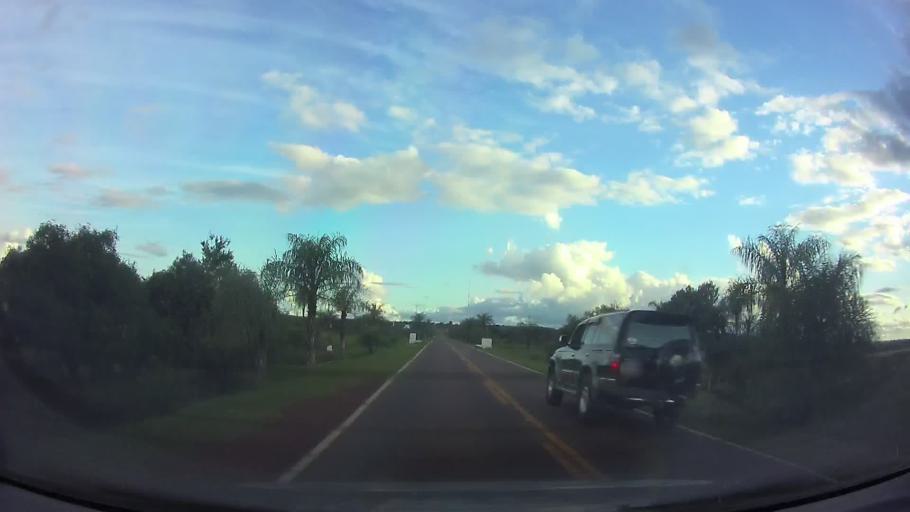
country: PY
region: Paraguari
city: Acahay
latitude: -25.8917
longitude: -57.1194
